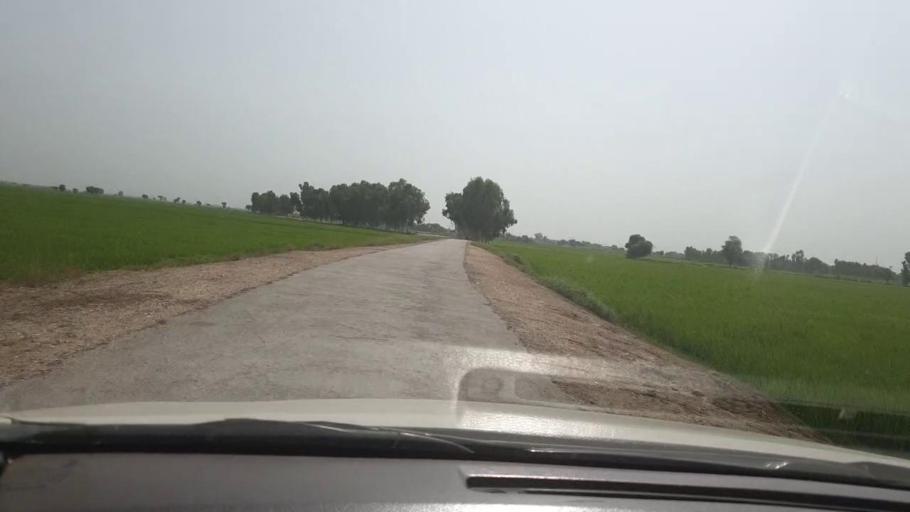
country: PK
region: Sindh
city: Rustam jo Goth
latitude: 27.9748
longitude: 68.7854
